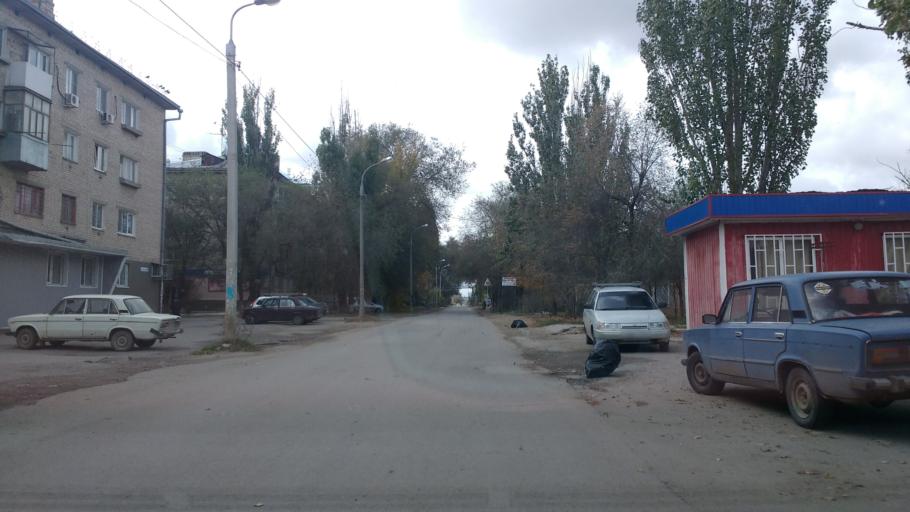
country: RU
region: Volgograd
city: Vodstroy
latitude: 48.7747
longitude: 44.5444
